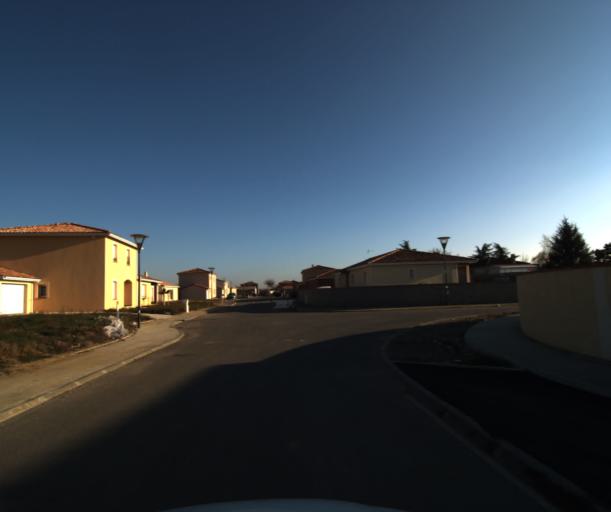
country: FR
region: Midi-Pyrenees
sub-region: Departement de la Haute-Garonne
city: Colomiers
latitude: 43.6249
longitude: 1.3273
